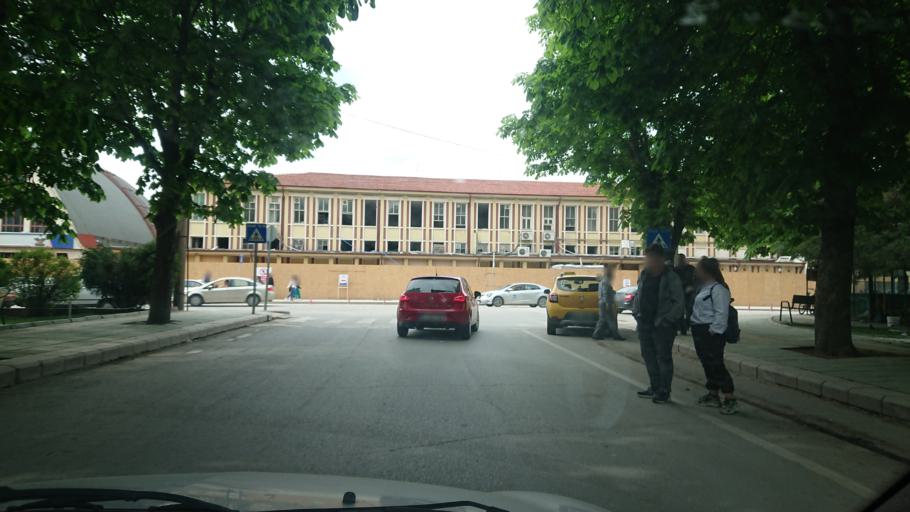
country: TR
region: Eskisehir
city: Eskisehir
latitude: 39.7790
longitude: 30.5083
